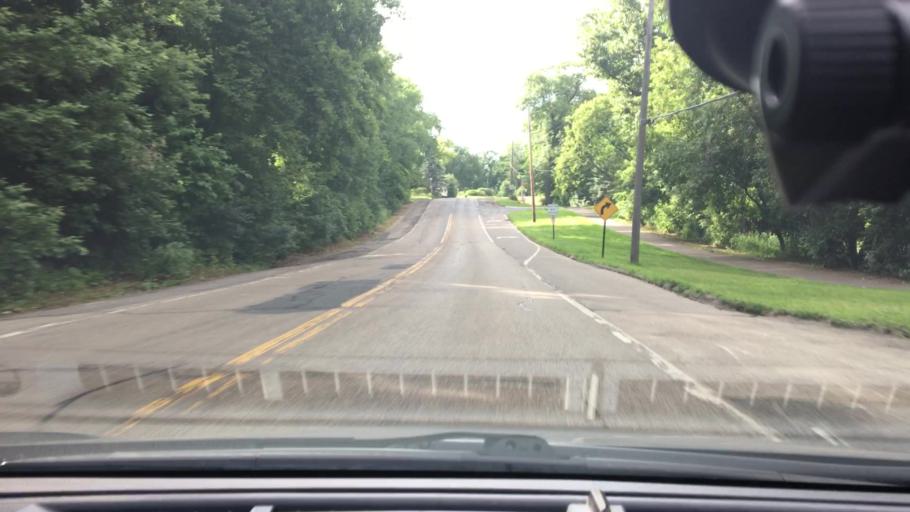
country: US
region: Minnesota
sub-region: Hennepin County
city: Plymouth
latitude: 45.0125
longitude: -93.4370
